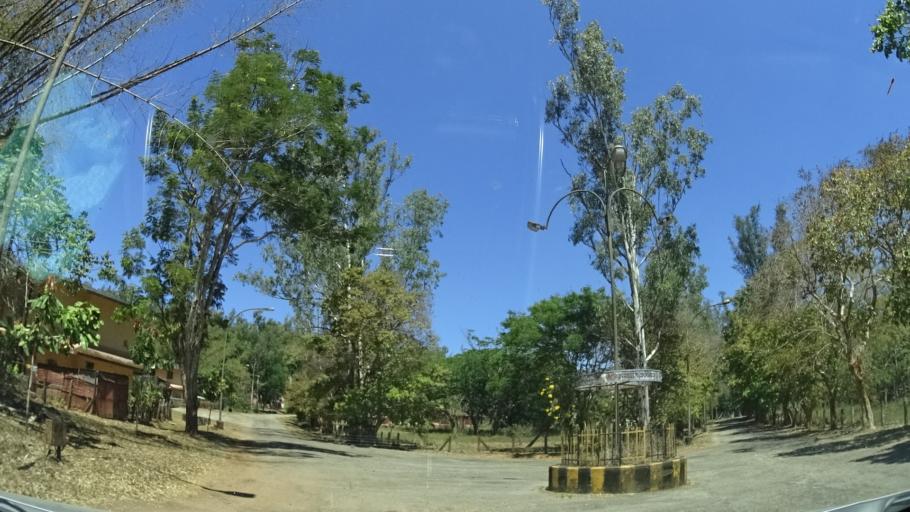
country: IN
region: Karnataka
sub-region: Chikmagalur
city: Sringeri
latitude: 13.2214
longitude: 75.2512
